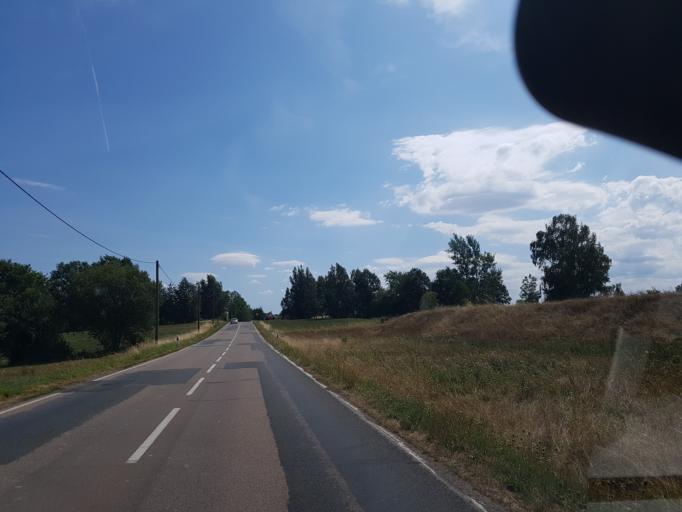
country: DE
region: Saxony
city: Hartha
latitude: 51.0850
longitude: 12.9878
